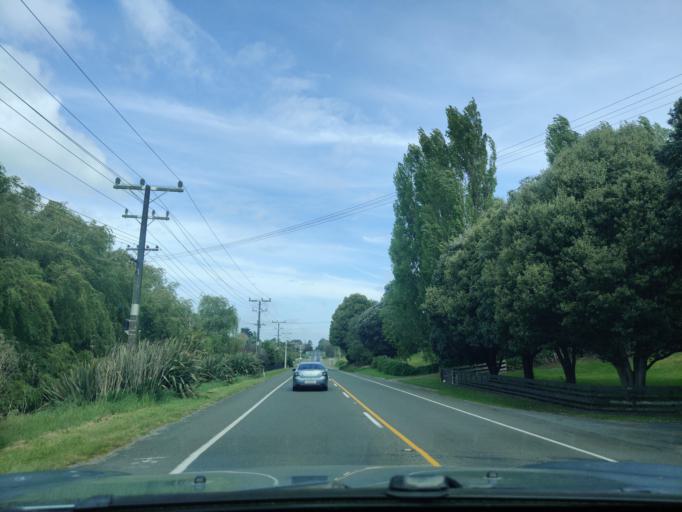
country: NZ
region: Manawatu-Wanganui
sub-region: Wanganui District
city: Wanganui
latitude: -39.9001
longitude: 175.0131
